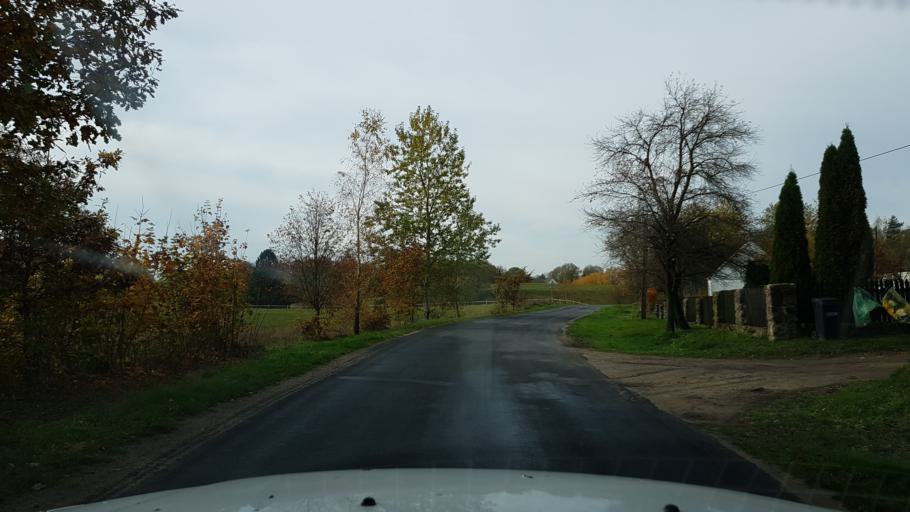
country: PL
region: West Pomeranian Voivodeship
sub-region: Powiat swidwinski
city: Polczyn-Zdroj
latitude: 53.7465
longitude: 16.0458
